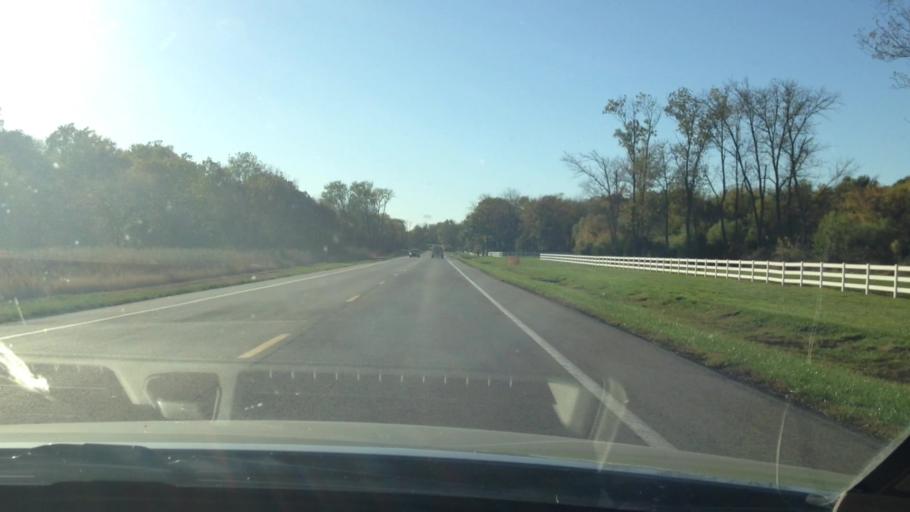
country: US
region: Kansas
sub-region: Johnson County
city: Edgerton
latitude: 38.7677
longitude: -94.9890
